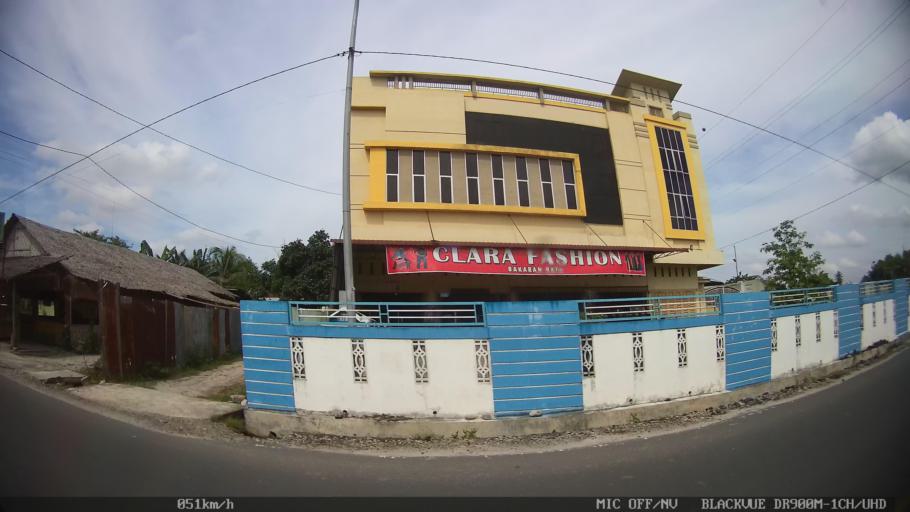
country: ID
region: North Sumatra
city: Percut
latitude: 3.5838
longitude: 98.8618
